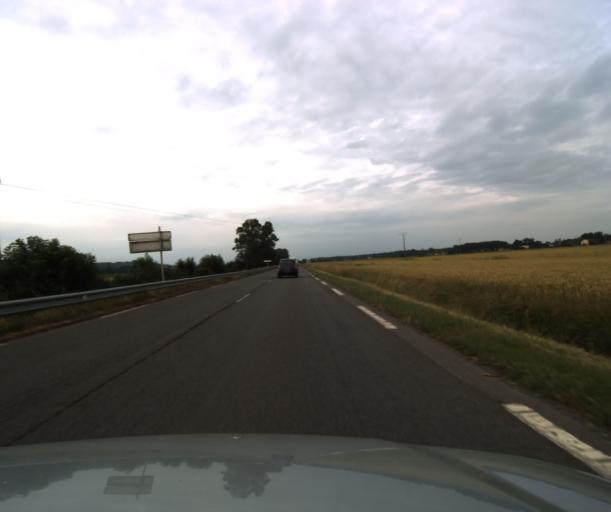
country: FR
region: Midi-Pyrenees
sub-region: Departement des Hautes-Pyrenees
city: Rabastens-de-Bigorre
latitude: 43.3547
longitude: 0.1383
